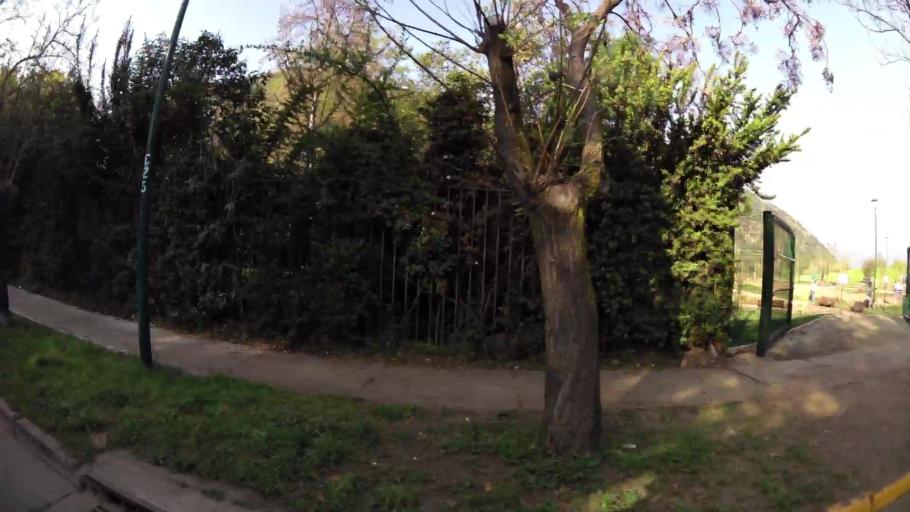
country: CL
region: Santiago Metropolitan
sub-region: Provincia de Santiago
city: Villa Presidente Frei, Nunoa, Santiago, Chile
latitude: -33.3465
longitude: -70.5398
